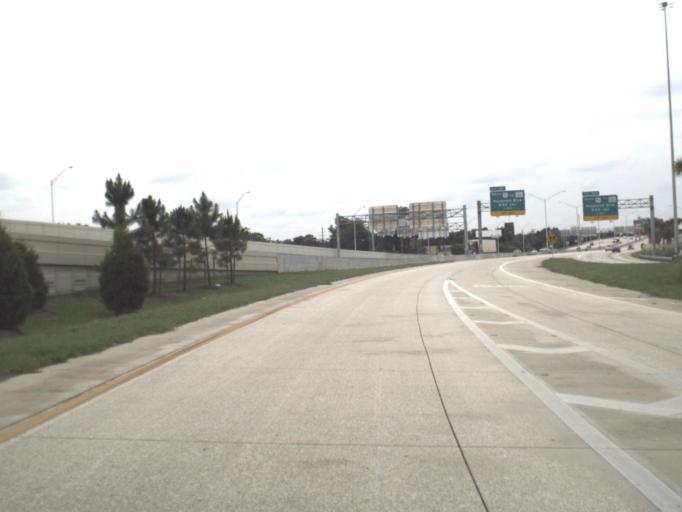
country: US
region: Florida
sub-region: Duval County
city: Jacksonville
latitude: 30.3211
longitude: -81.6840
